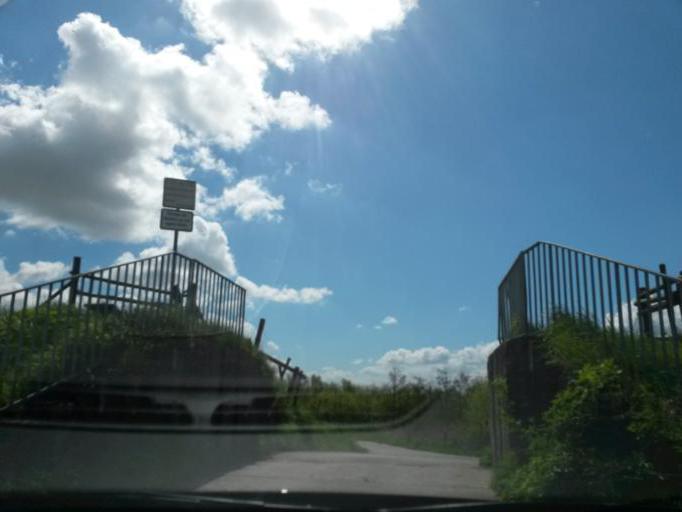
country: DE
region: Schleswig-Holstein
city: Seestermuhe
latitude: 53.6824
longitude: 9.5752
